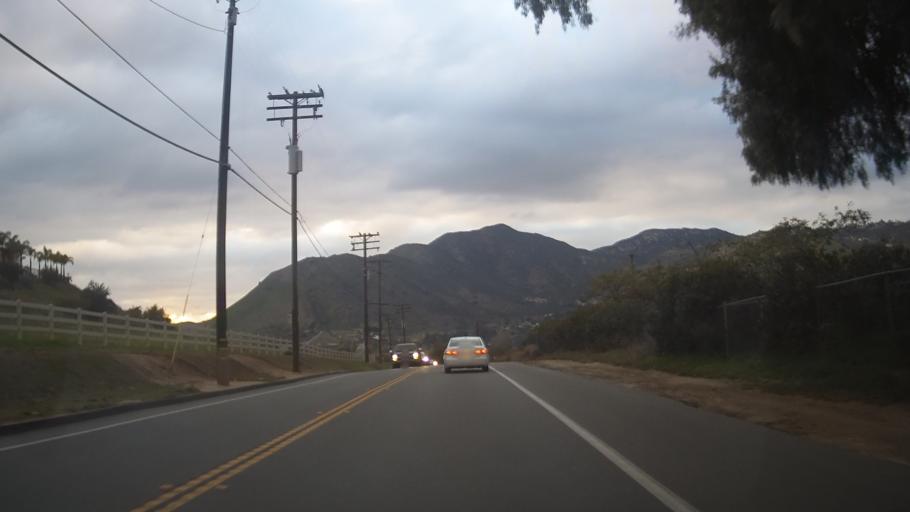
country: US
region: California
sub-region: San Diego County
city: Granite Hills
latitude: 32.7748
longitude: -116.8876
